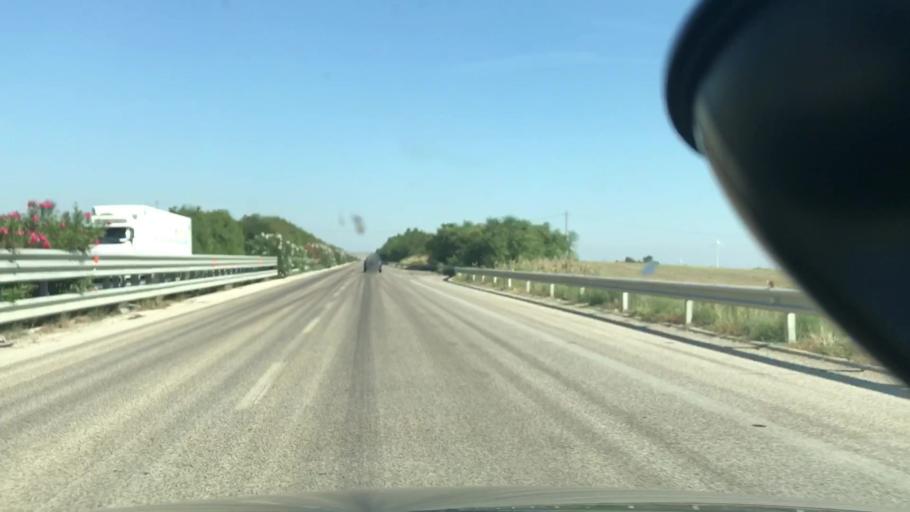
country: IT
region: Apulia
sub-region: Provincia di Foggia
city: Ascoli Satriano
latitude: 41.2812
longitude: 15.5540
